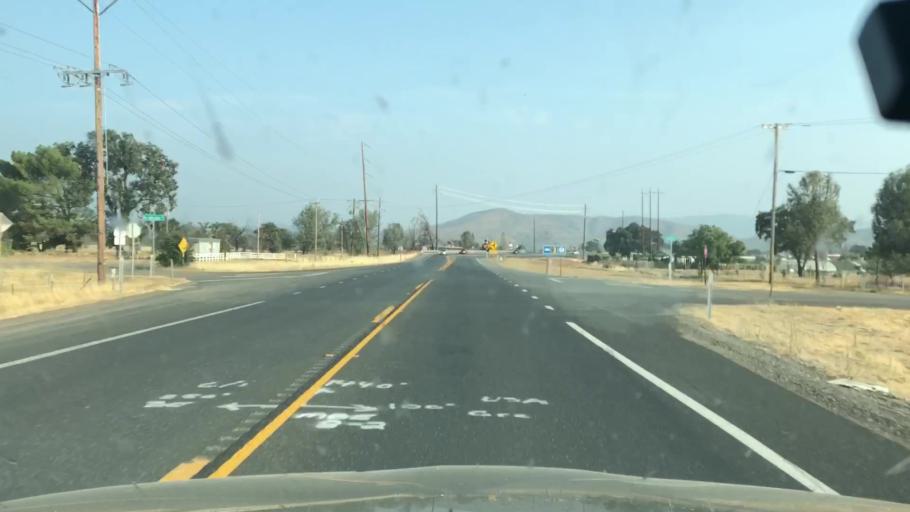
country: US
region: California
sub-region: Lake County
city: Hidden Valley Lake
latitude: 38.7954
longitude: -122.5674
